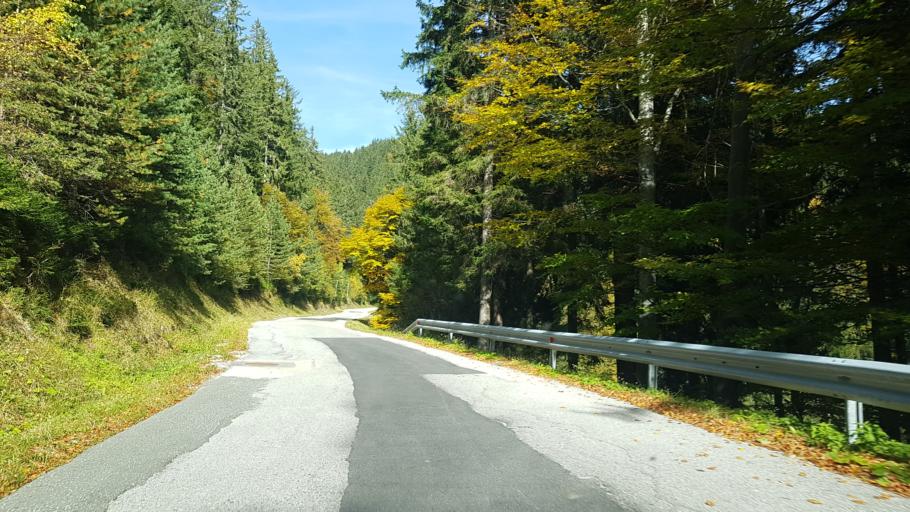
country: SI
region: Slovenj Gradec
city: Legen
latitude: 46.4969
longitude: 15.1923
